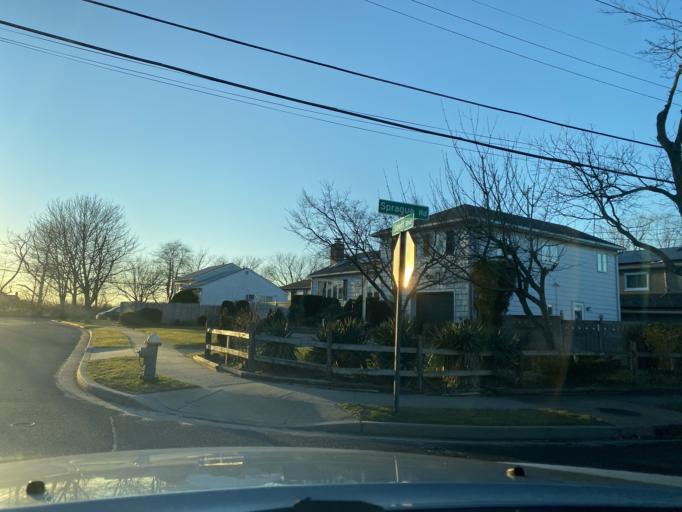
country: US
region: New York
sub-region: Nassau County
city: Inwood
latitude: 40.6237
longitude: -73.7506
